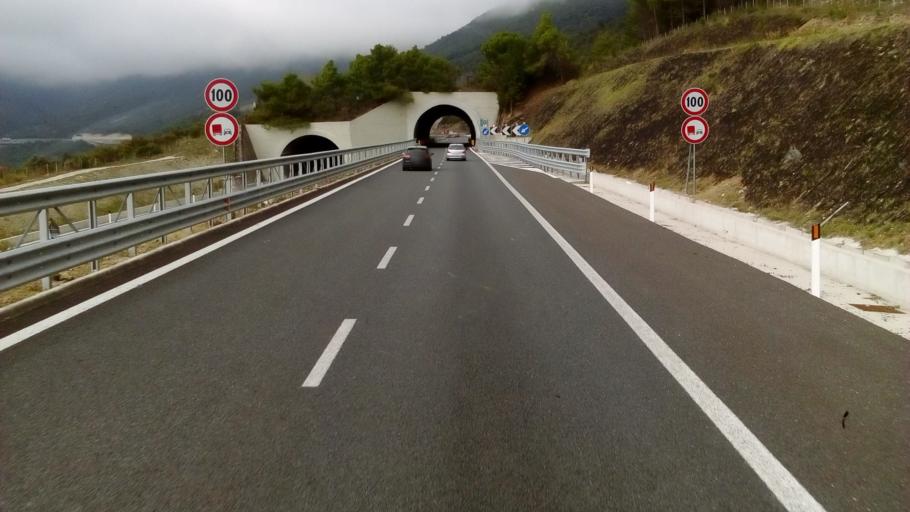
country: IT
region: Calabria
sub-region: Provincia di Cosenza
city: Morano Calabro
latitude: 39.8816
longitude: 16.1620
